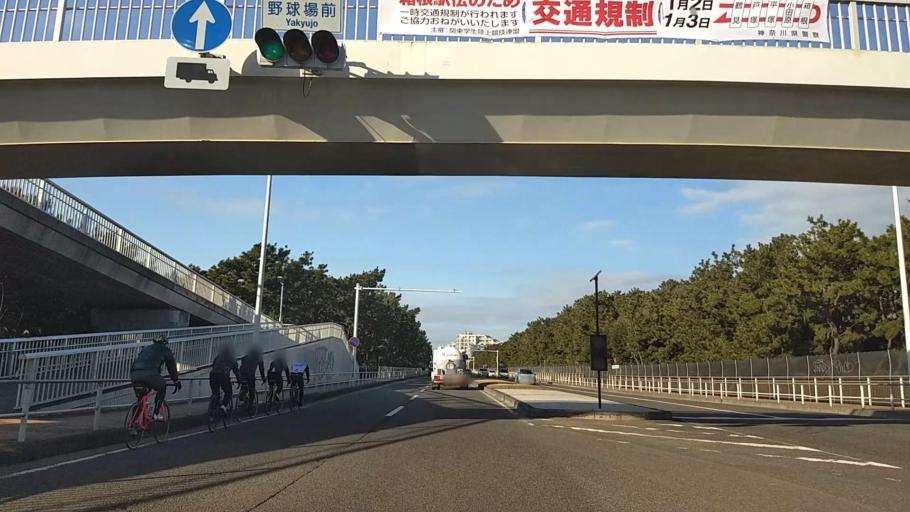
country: JP
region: Kanagawa
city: Chigasaki
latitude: 35.3187
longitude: 139.4063
